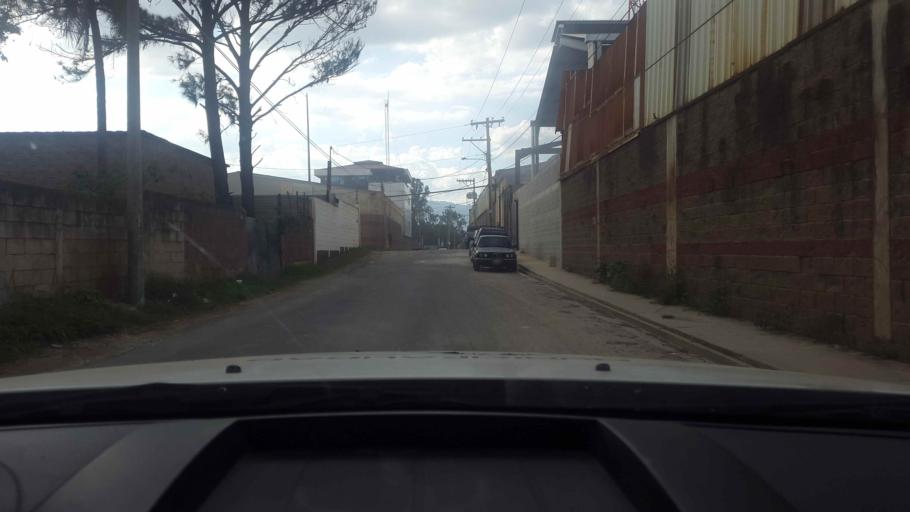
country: GT
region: Guatemala
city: Petapa
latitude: 14.5096
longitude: -90.5391
